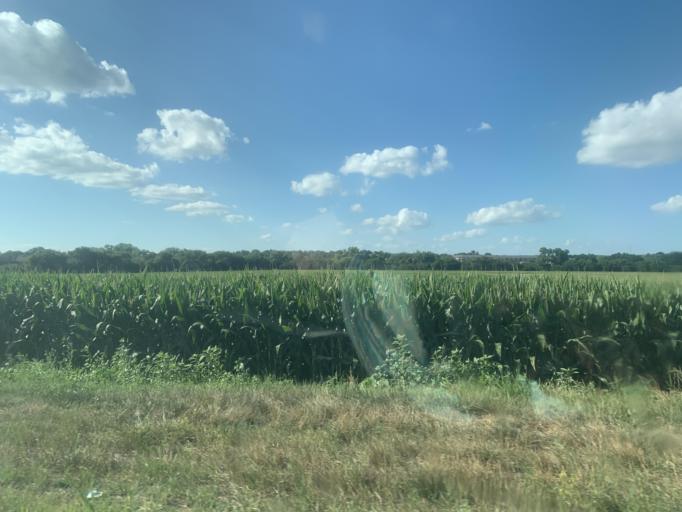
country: US
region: Nebraska
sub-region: Sarpy County
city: Chalco
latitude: 41.1763
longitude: -96.1421
